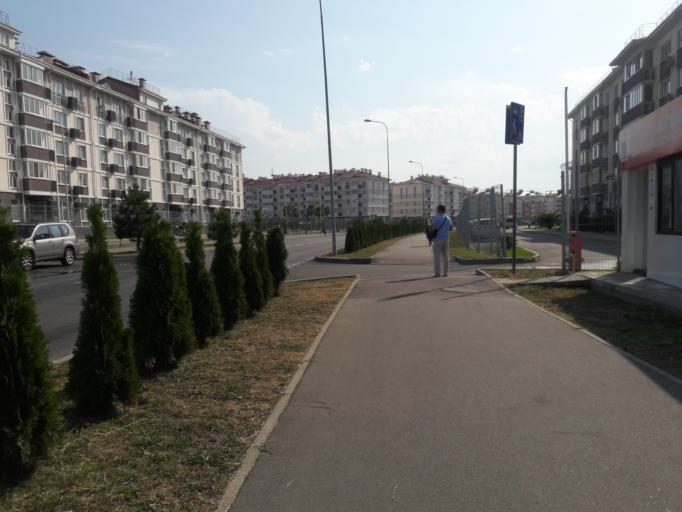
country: RU
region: Krasnodarskiy
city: Vysokoye
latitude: 43.3933
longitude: 39.9954
